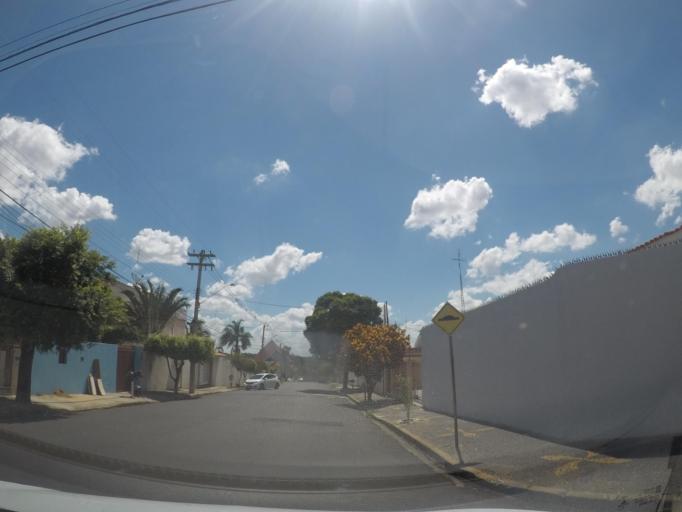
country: BR
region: Sao Paulo
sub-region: Sumare
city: Sumare
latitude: -22.8258
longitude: -47.2745
